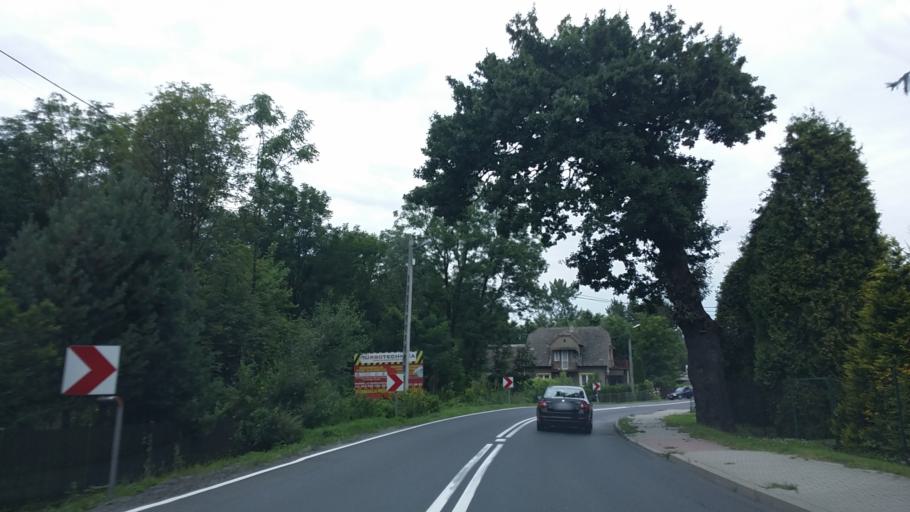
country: PL
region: Lesser Poland Voivodeship
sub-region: Powiat wadowicki
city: Ryczow
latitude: 49.9740
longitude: 19.5607
